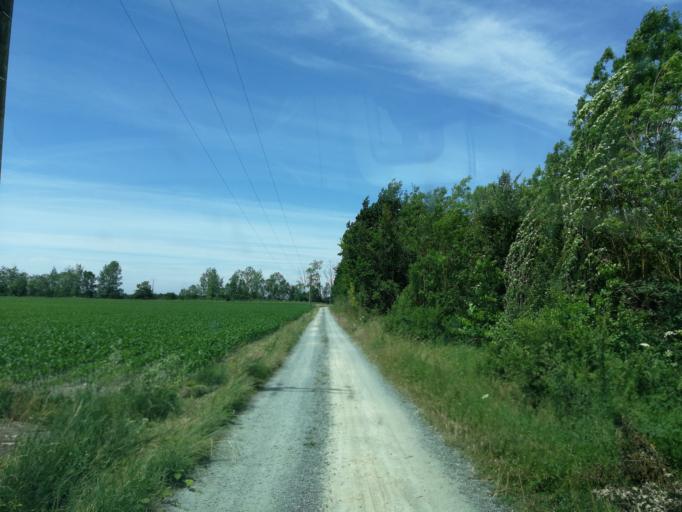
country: FR
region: Poitou-Charentes
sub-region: Departement de la Charente-Maritime
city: Marans
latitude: 46.3659
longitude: -0.9591
